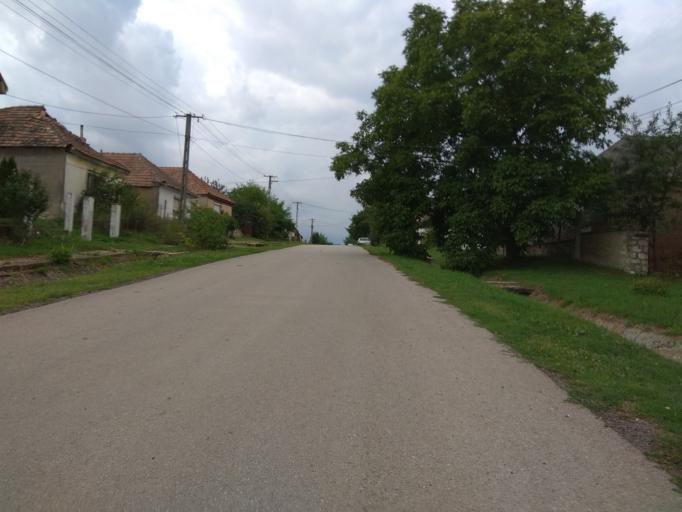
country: HU
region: Borsod-Abauj-Zemplen
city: Monok
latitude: 48.2092
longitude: 21.1432
